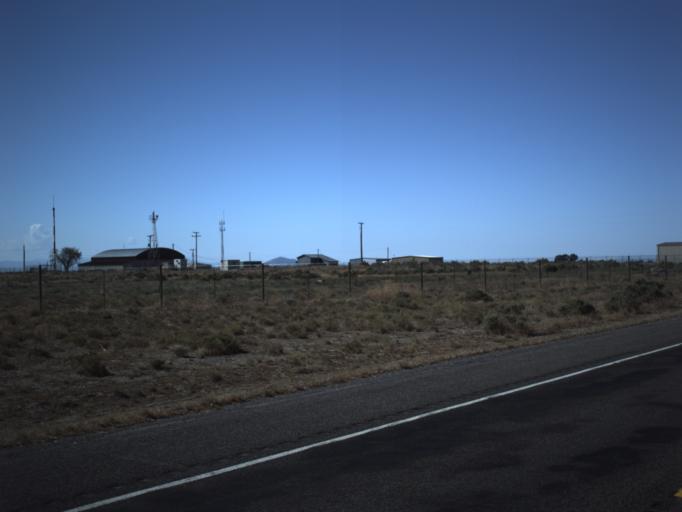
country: US
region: Utah
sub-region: Millard County
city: Delta
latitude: 39.3896
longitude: -112.5132
